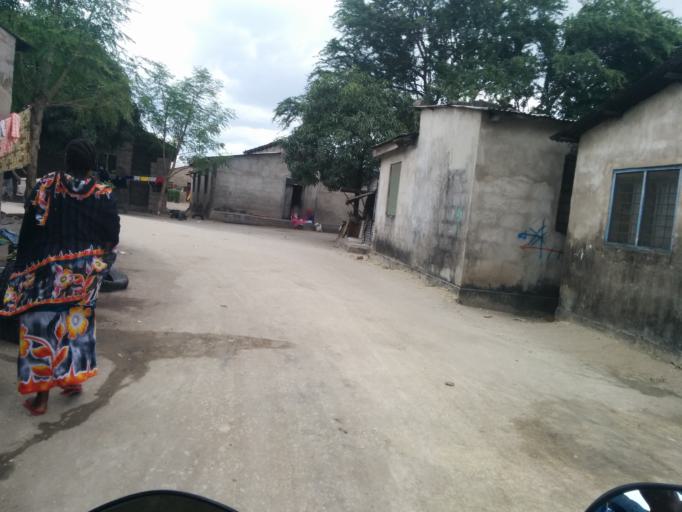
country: TZ
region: Dar es Salaam
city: Dar es Salaam
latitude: -6.8726
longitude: 39.2464
